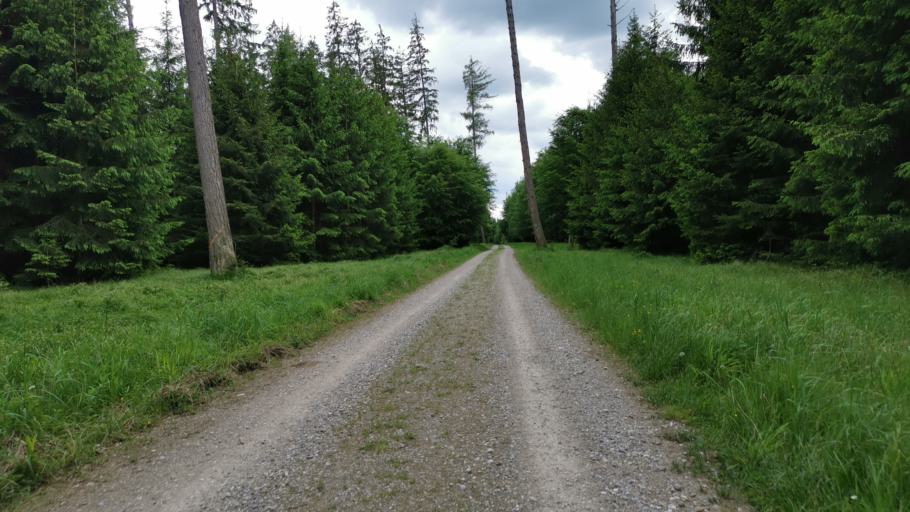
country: DE
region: Bavaria
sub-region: Upper Bavaria
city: Baierbrunn
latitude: 48.0357
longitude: 11.4677
